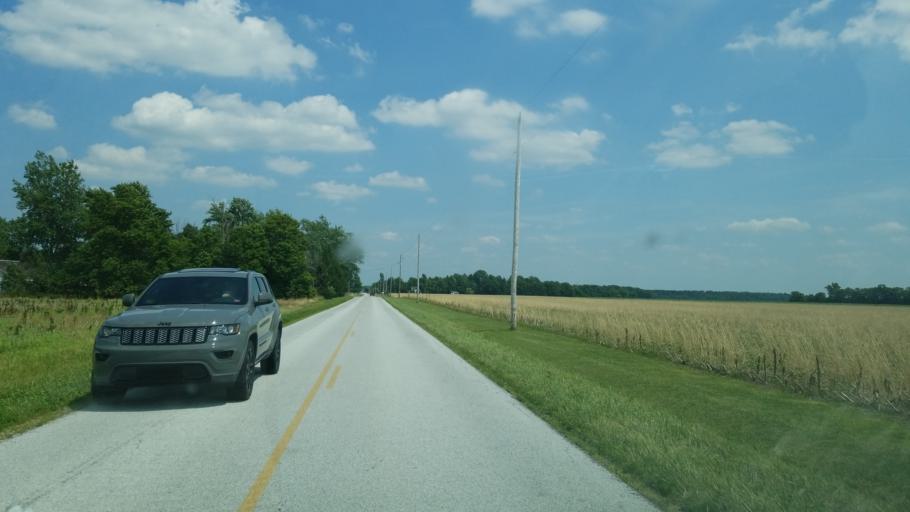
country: US
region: Ohio
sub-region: Seneca County
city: Tiffin
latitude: 41.1666
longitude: -83.2414
